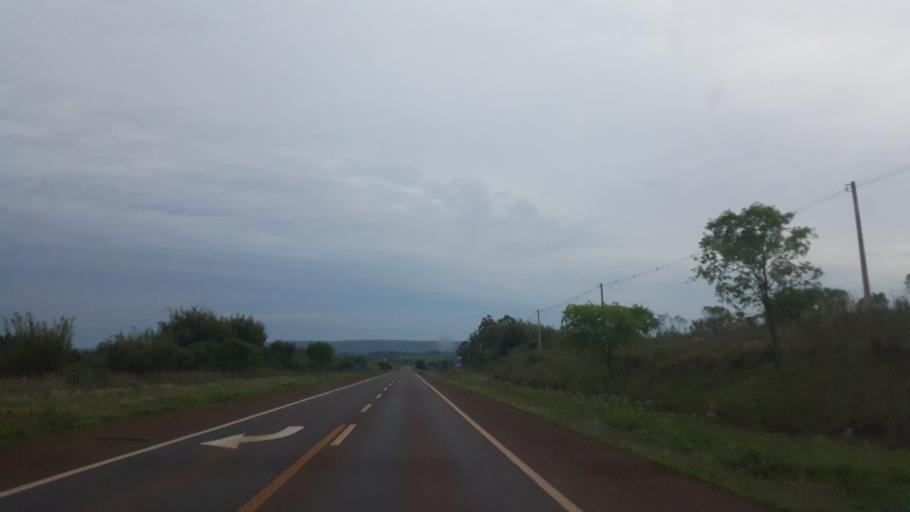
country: AR
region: Misiones
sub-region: Departamento de Apostoles
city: San Jose
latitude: -27.7770
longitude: -55.8101
